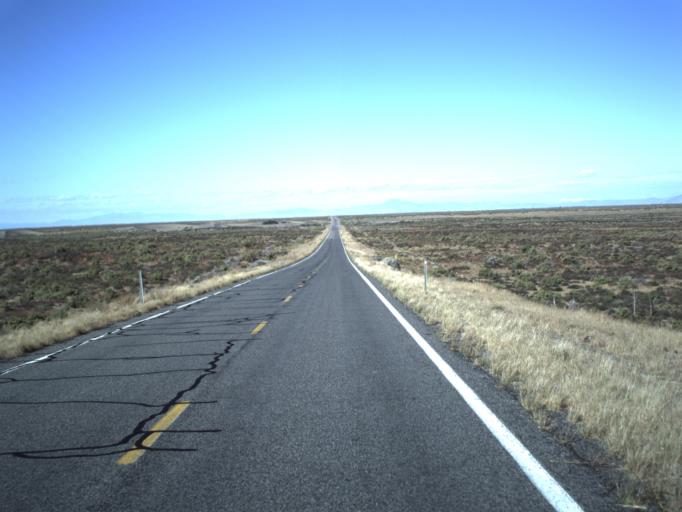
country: US
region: Utah
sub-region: Millard County
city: Delta
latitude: 39.3547
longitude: -112.3876
